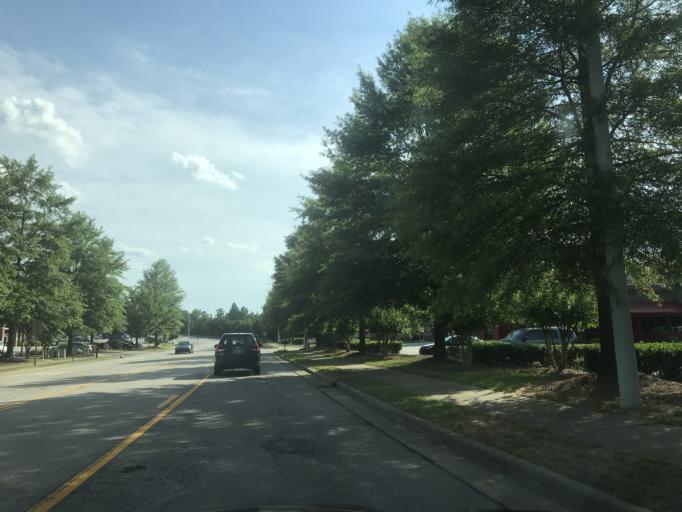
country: US
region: North Carolina
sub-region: Wake County
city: Wake Forest
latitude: 35.9678
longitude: -78.5427
